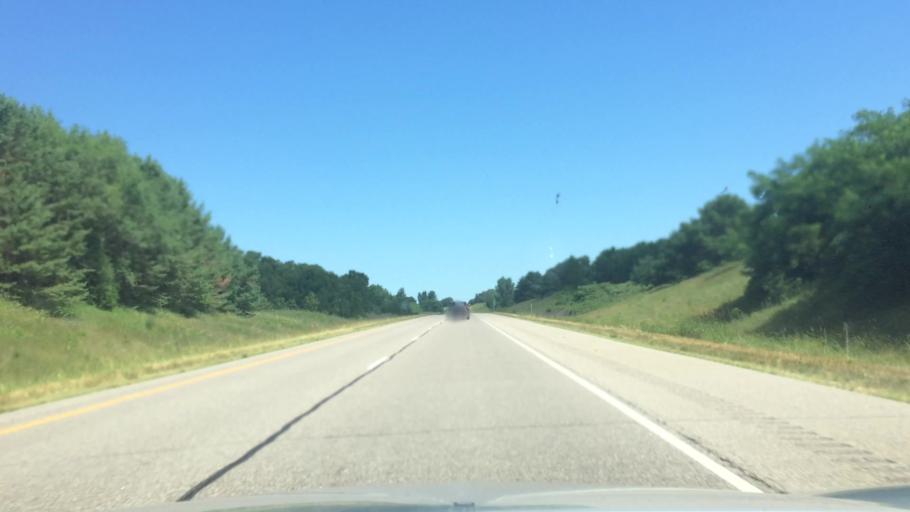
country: US
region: Wisconsin
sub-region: Marquette County
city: Westfield
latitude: 44.0856
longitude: -89.5319
